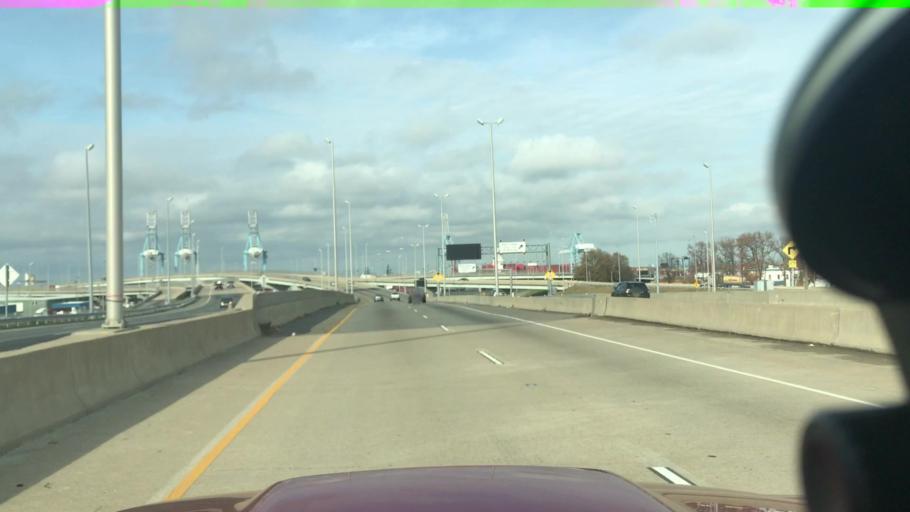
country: US
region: Virginia
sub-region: City of Portsmouth
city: Portsmouth
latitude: 36.8471
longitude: -76.3294
